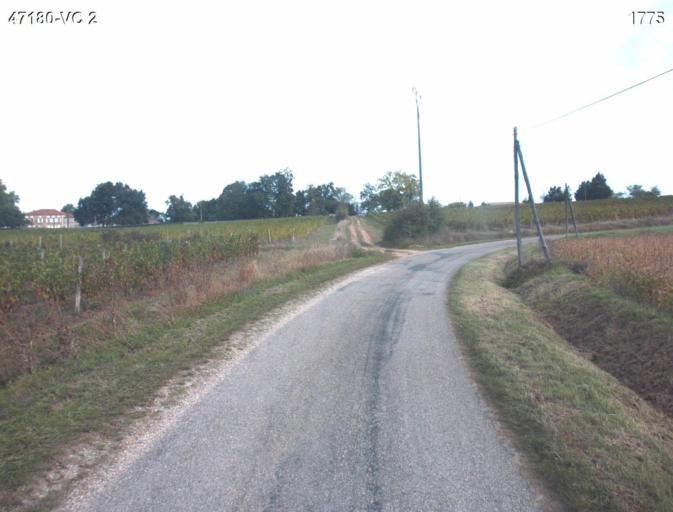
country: FR
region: Aquitaine
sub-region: Departement du Lot-et-Garonne
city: Sainte-Colombe-en-Bruilhois
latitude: 44.1709
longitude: 0.4373
